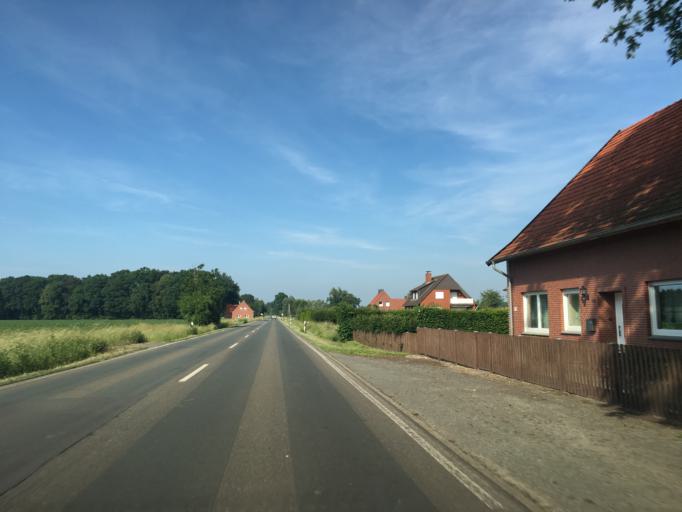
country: DE
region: North Rhine-Westphalia
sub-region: Regierungsbezirk Munster
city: Nordwalde
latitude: 52.0847
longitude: 7.5321
